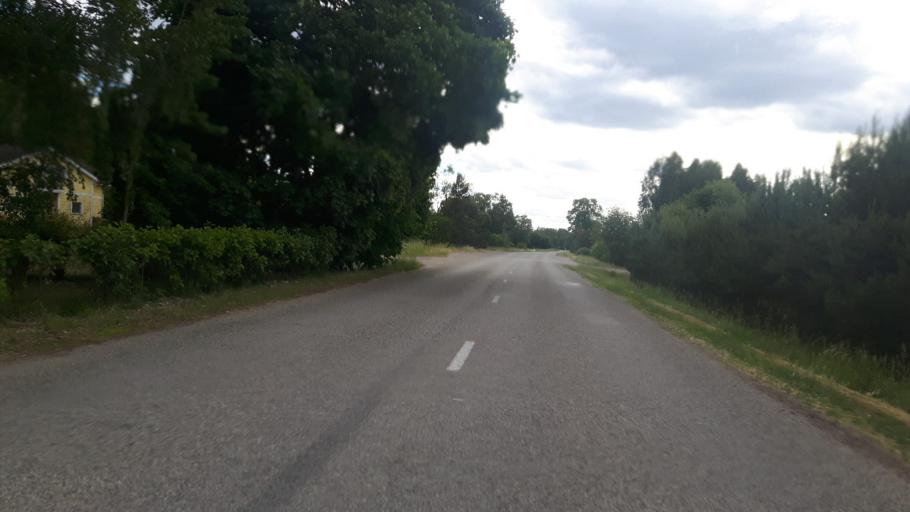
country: LV
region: Engure
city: Smarde
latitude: 57.0365
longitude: 23.3722
